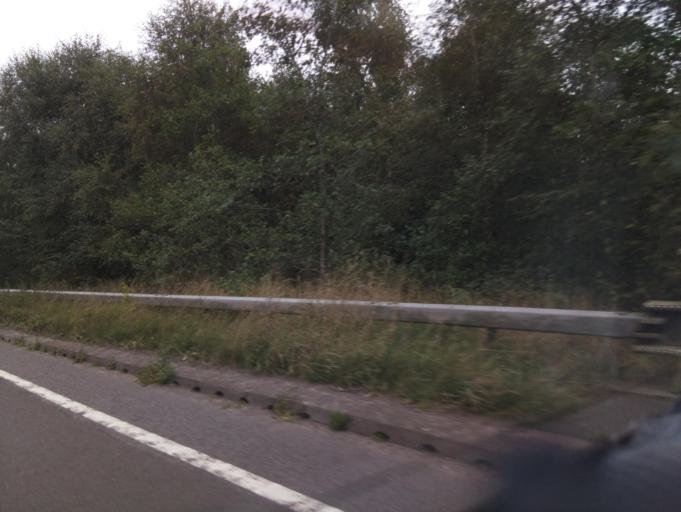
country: GB
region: England
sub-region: Shropshire
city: Stoke upon Tern
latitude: 52.8637
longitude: -2.5554
